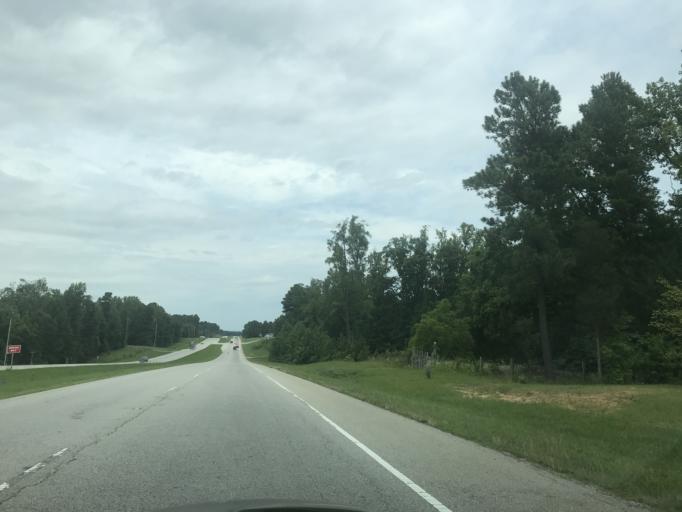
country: US
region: North Carolina
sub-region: Franklin County
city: Franklinton
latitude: 36.1397
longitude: -78.4502
